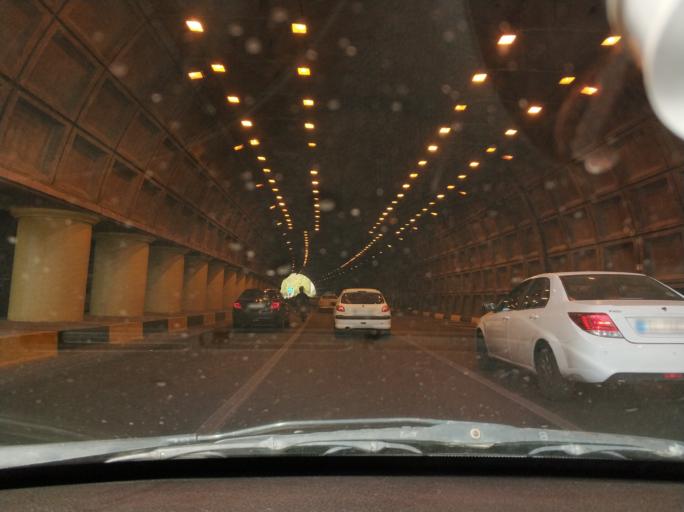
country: IR
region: Tehran
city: Tehran
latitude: 35.7441
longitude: 51.4062
